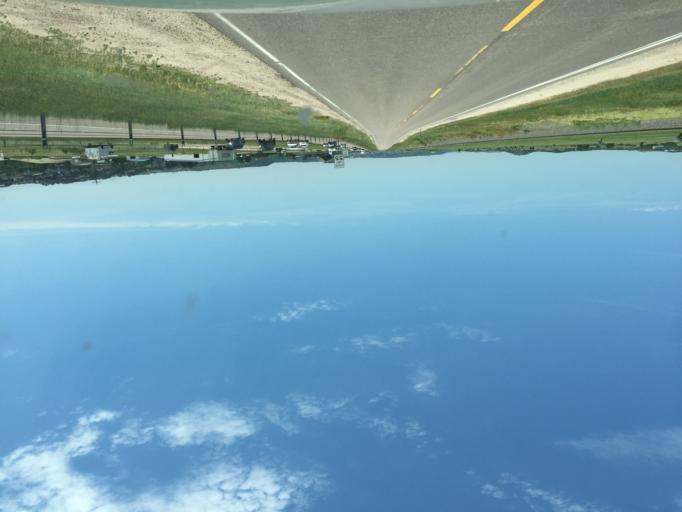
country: US
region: Colorado
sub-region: Douglas County
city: Castle Rock
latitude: 39.3295
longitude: -104.8797
